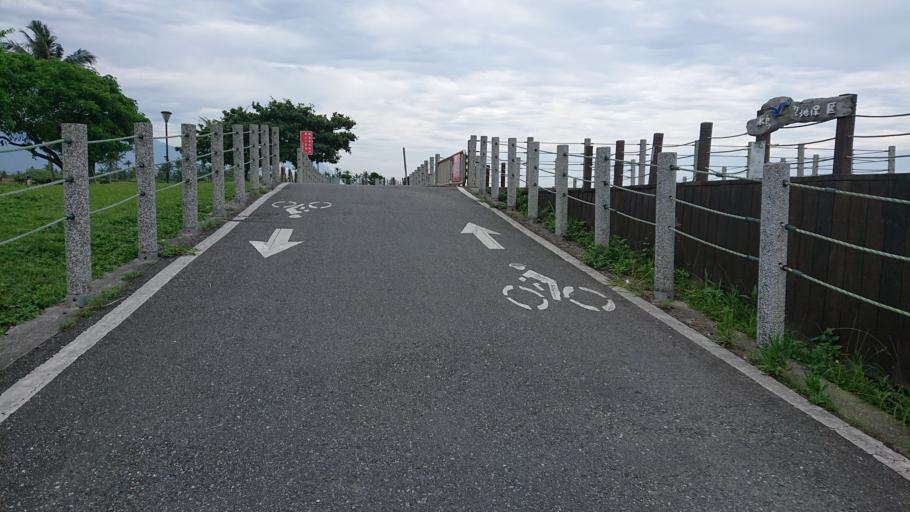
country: TW
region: Taiwan
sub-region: Hualien
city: Hualian
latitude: 23.9374
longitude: 121.6026
